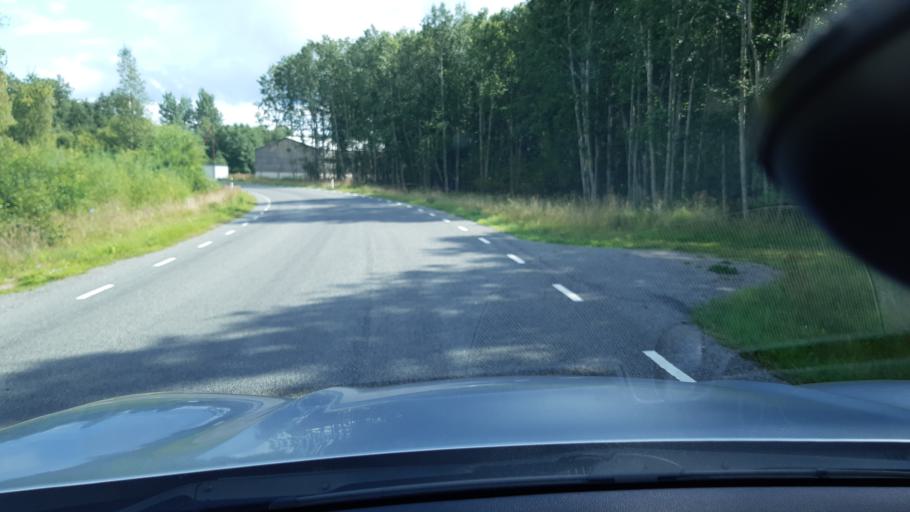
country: EE
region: Raplamaa
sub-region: Kehtna vald
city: Kehtna
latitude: 58.8729
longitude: 25.0010
